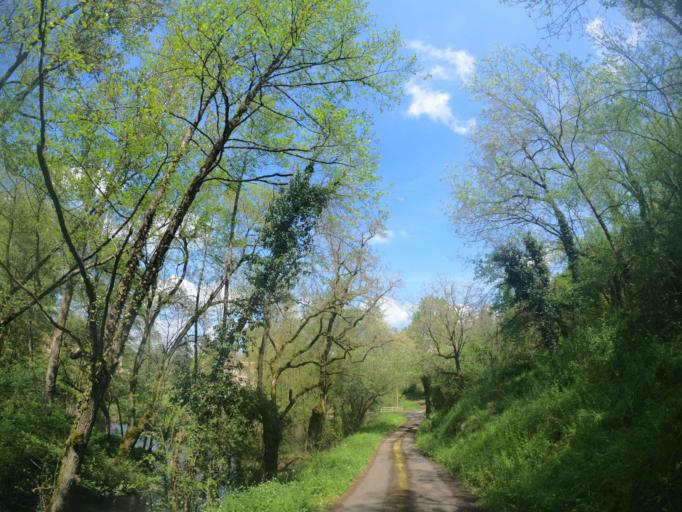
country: FR
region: Poitou-Charentes
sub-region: Departement des Deux-Sevres
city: Saint-Varent
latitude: 46.8703
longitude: -0.2449
